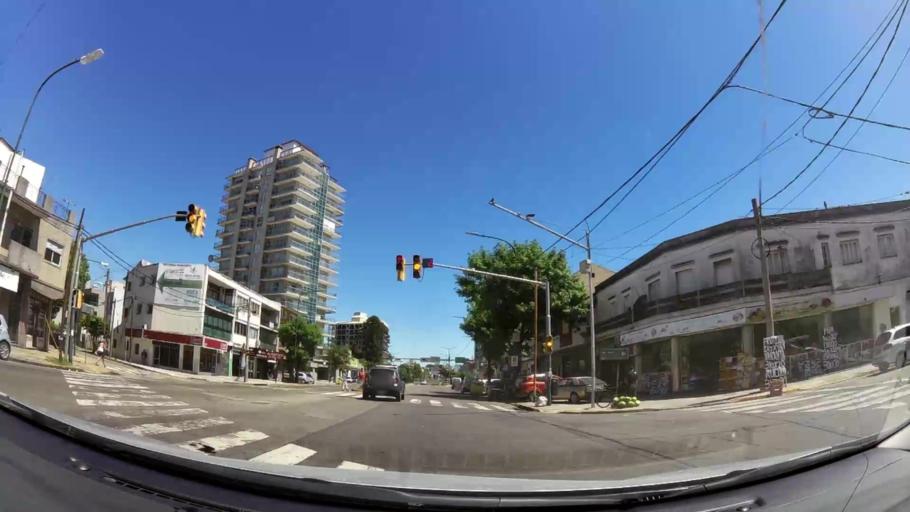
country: AR
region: Buenos Aires
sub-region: Partido de San Isidro
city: San Isidro
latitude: -34.4584
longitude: -58.5312
